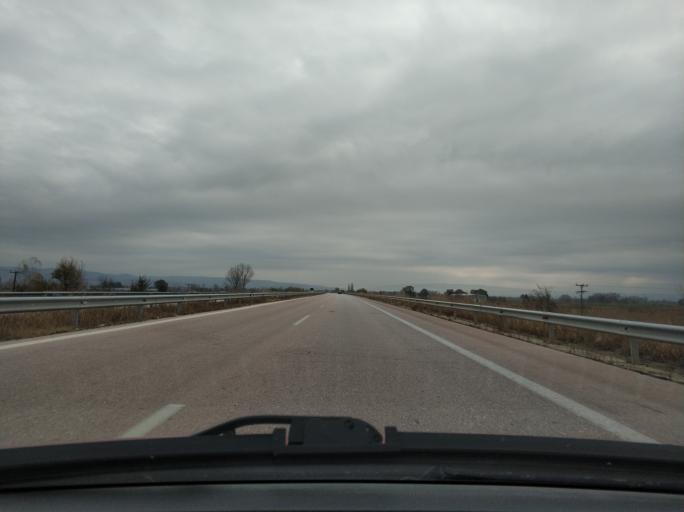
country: GR
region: Central Macedonia
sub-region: Nomos Thessalonikis
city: Lagkadas
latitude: 40.7271
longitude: 23.0720
